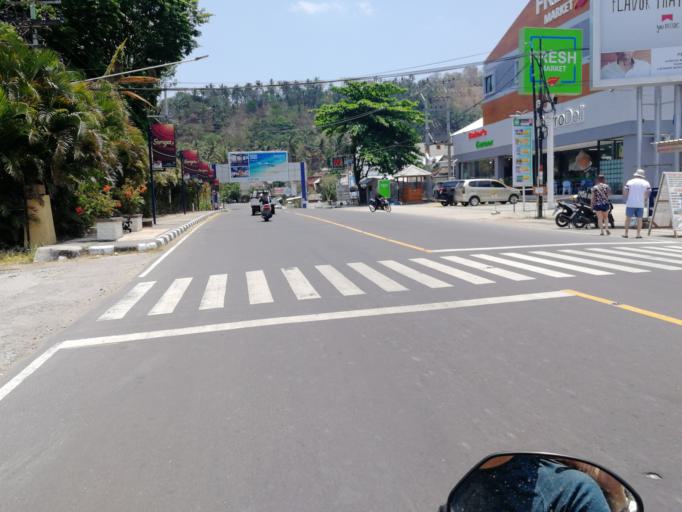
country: ID
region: West Nusa Tenggara
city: Mambalan
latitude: -8.4974
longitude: 116.0488
